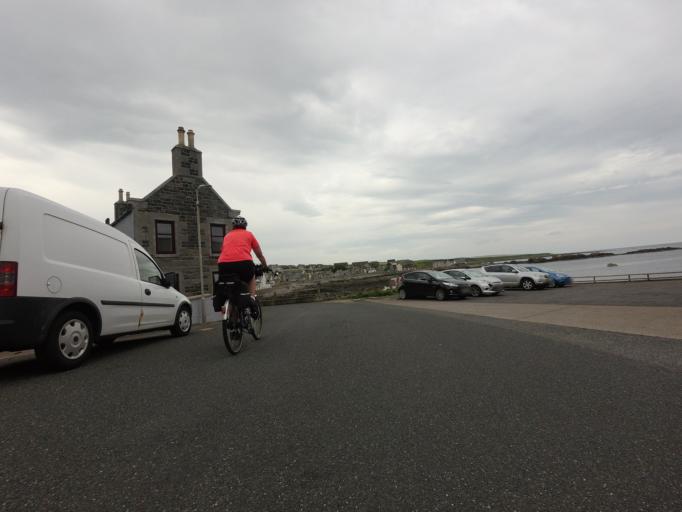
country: GB
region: Scotland
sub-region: Aberdeenshire
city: Whitehills
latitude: 57.6784
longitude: -2.5806
